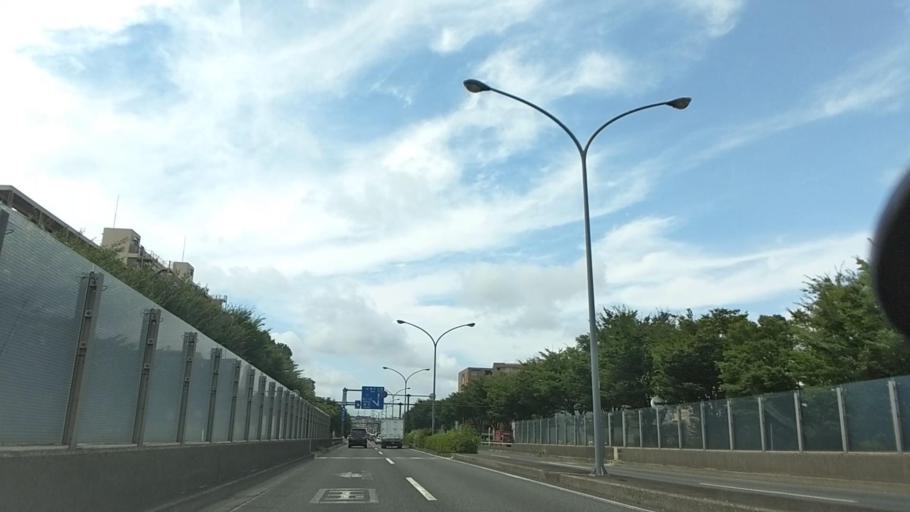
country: JP
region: Kanagawa
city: Yokohama
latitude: 35.4250
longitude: 139.5613
